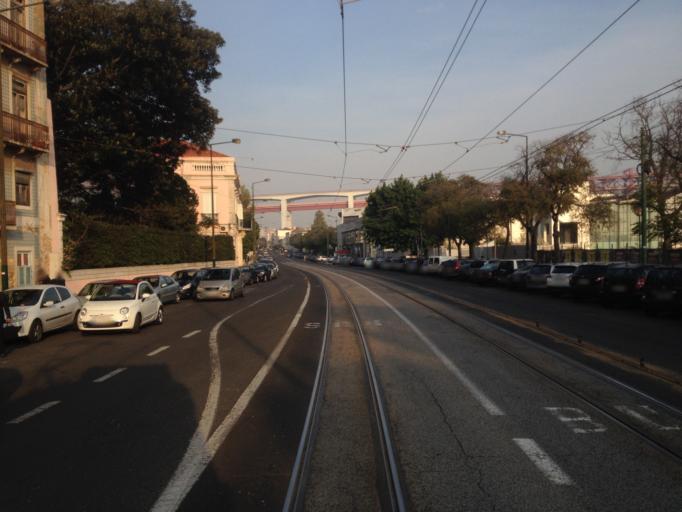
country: PT
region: Setubal
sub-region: Almada
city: Pragal
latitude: 38.6987
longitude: -9.1871
